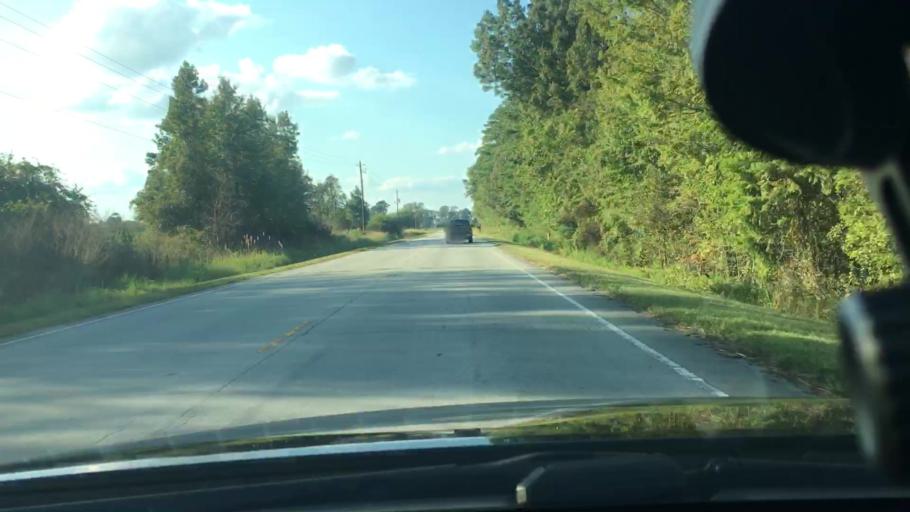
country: US
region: North Carolina
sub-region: Craven County
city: Vanceboro
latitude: 35.3693
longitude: -77.2055
